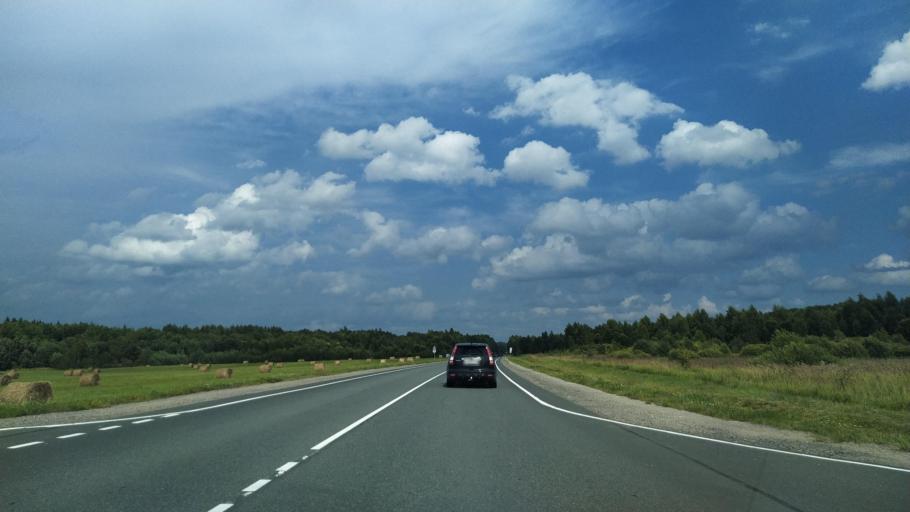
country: RU
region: Pskov
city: Porkhov
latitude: 57.8565
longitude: 29.5571
